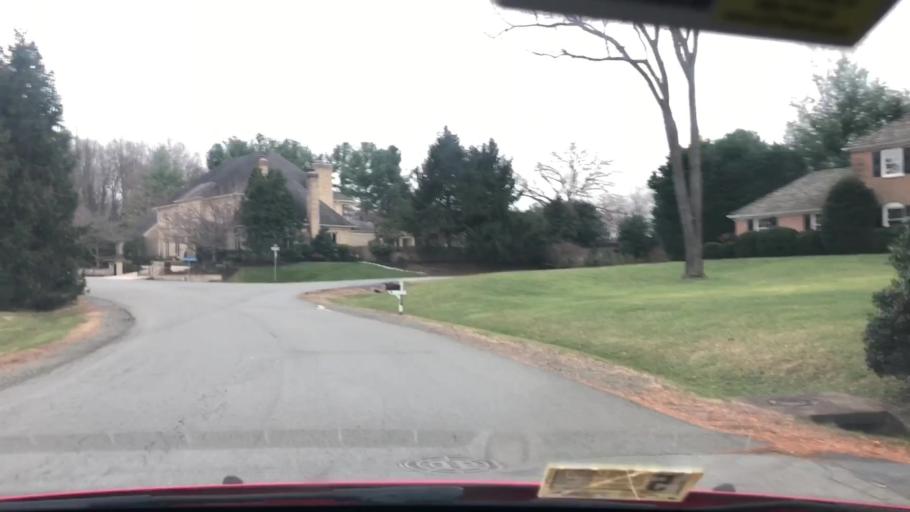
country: US
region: Virginia
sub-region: Fairfax County
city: Wolf Trap
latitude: 38.9672
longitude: -77.2742
